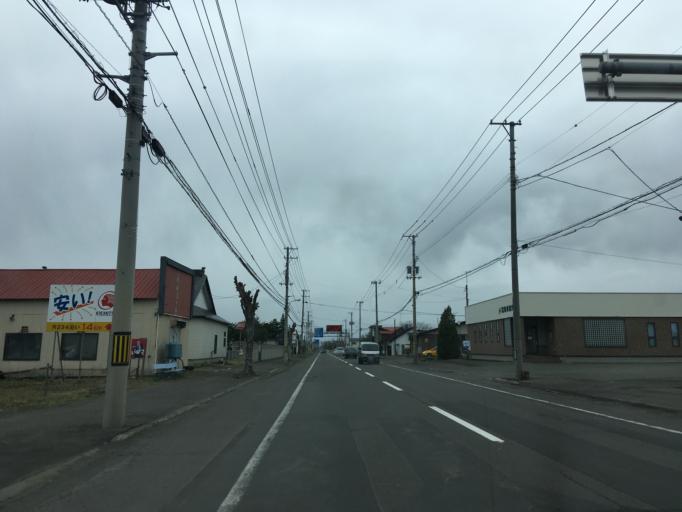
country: JP
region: Hokkaido
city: Chitose
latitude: 42.9457
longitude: 141.8035
